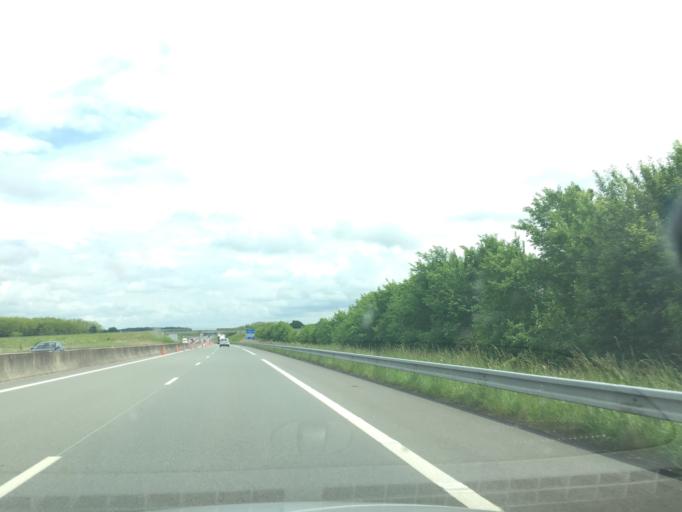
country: FR
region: Centre
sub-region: Departement d'Indre-et-Loire
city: Saint-Christophe-sur-le-Nais
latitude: 47.6519
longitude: 0.4540
